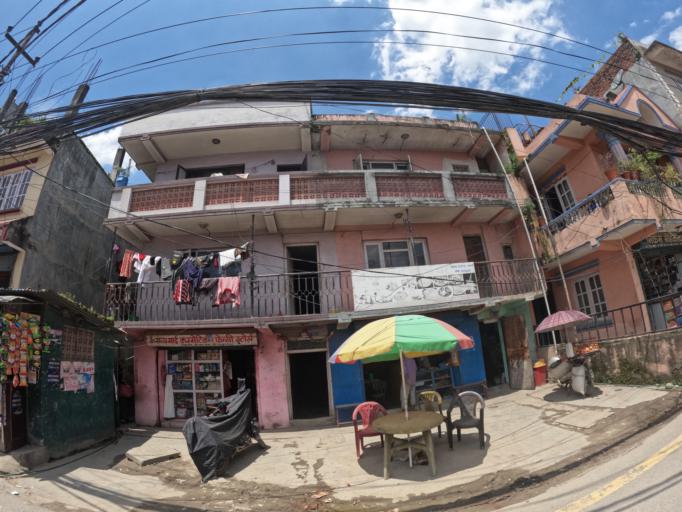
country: NP
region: Central Region
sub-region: Bagmati Zone
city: Kathmandu
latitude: 27.7416
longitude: 85.3217
